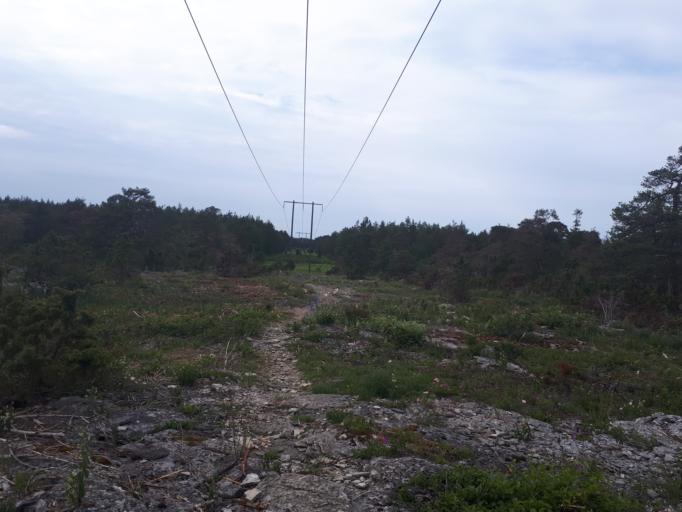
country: SE
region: Gotland
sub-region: Gotland
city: Visby
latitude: 57.6025
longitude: 18.3065
